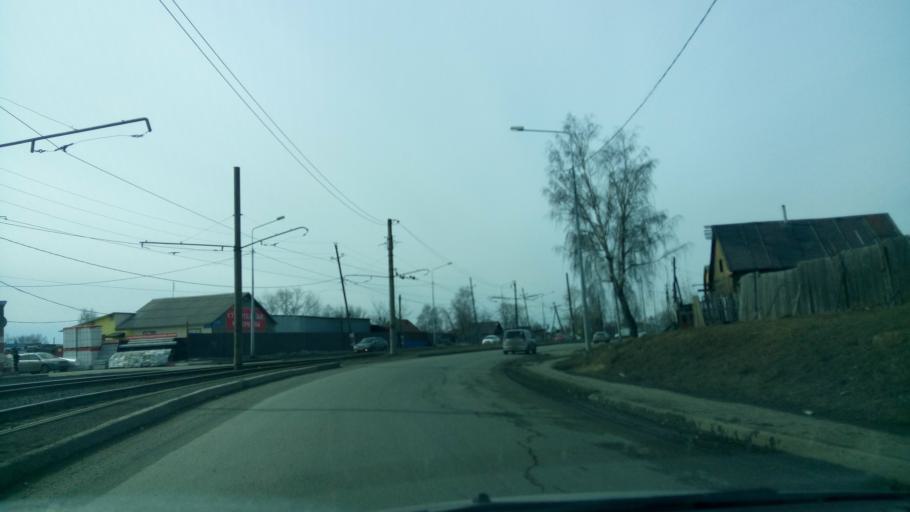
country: RU
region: Sverdlovsk
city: Nizhniy Tagil
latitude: 57.9013
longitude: 60.0088
